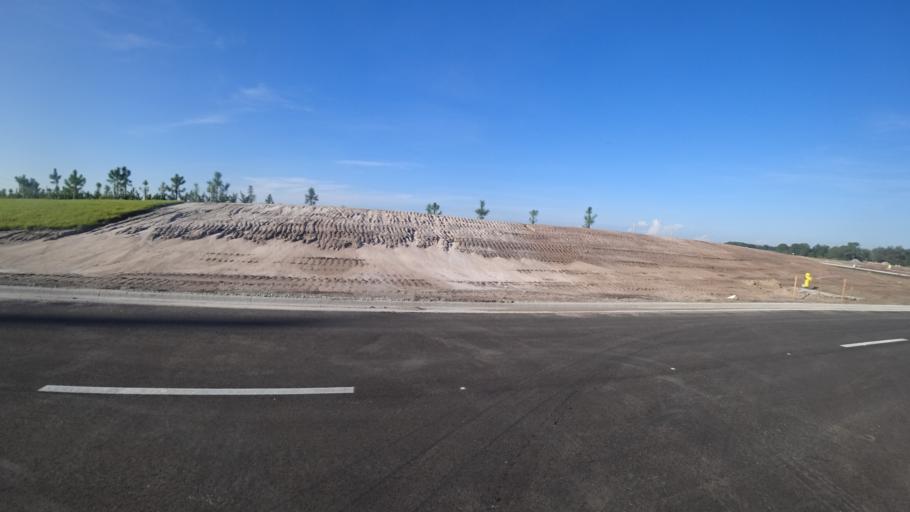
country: US
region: Florida
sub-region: Sarasota County
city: The Meadows
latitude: 27.4337
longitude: -82.3523
